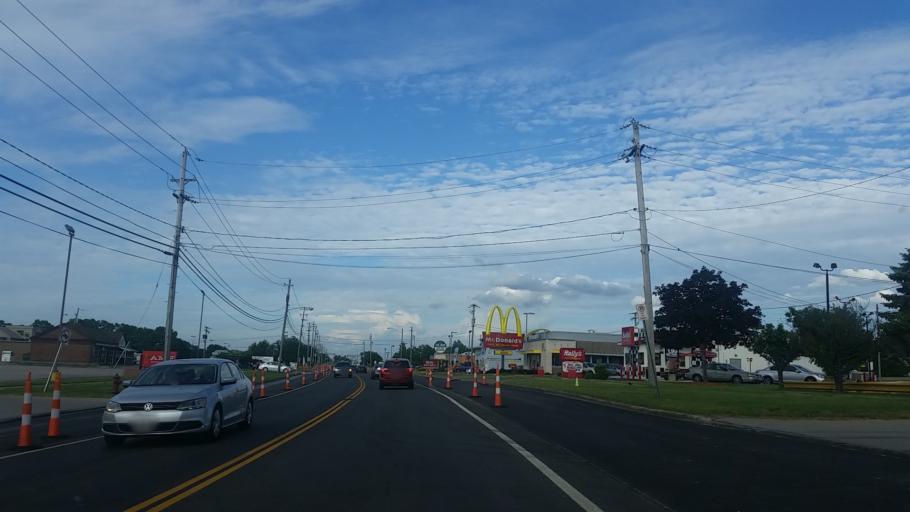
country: US
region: Ohio
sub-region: Cuyahoga County
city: Brook Park
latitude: 41.4038
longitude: -81.8011
